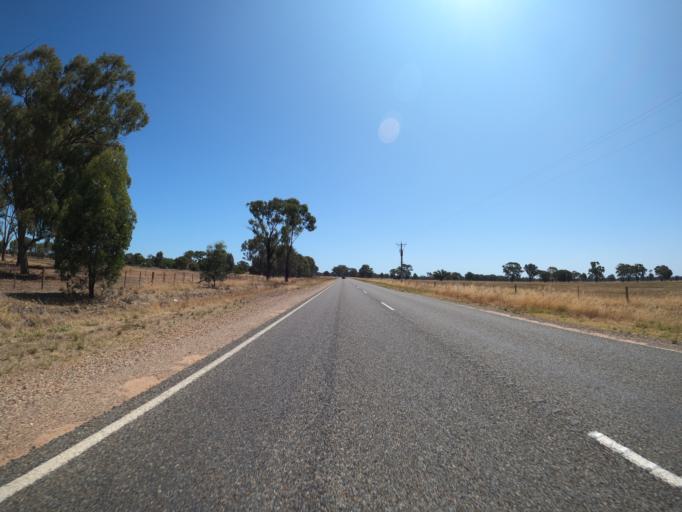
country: AU
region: New South Wales
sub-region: Corowa Shire
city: Corowa
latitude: -36.0661
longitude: 146.3675
